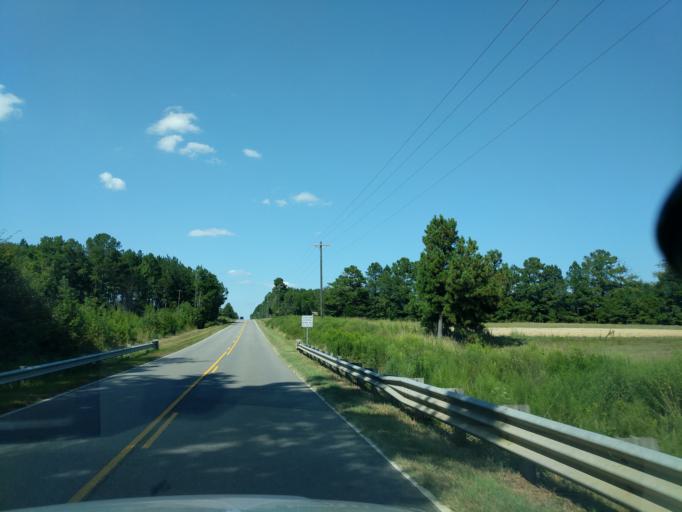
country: US
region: South Carolina
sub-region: Lexington County
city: Leesville
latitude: 33.9686
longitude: -81.5290
